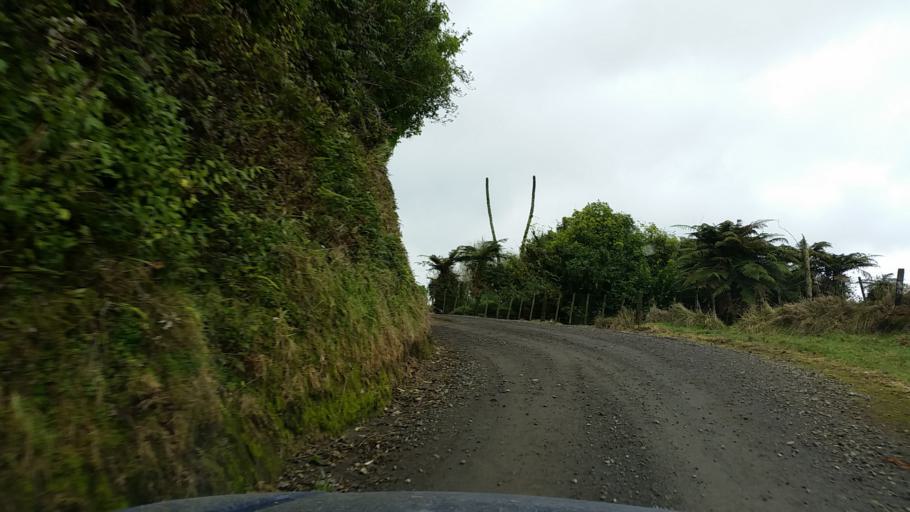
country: NZ
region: Taranaki
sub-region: South Taranaki District
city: Eltham
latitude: -39.1688
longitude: 174.6282
